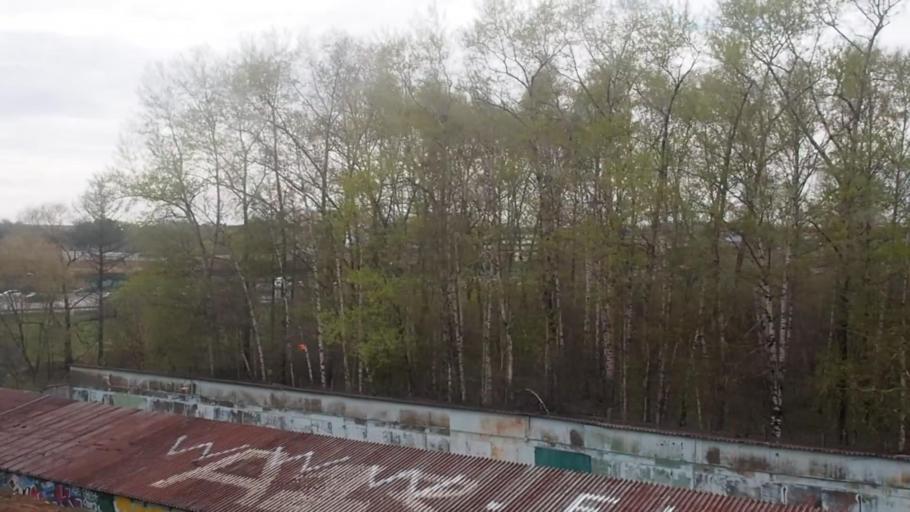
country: RU
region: Moskovskaya
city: Marfino
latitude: 55.7197
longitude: 37.3856
